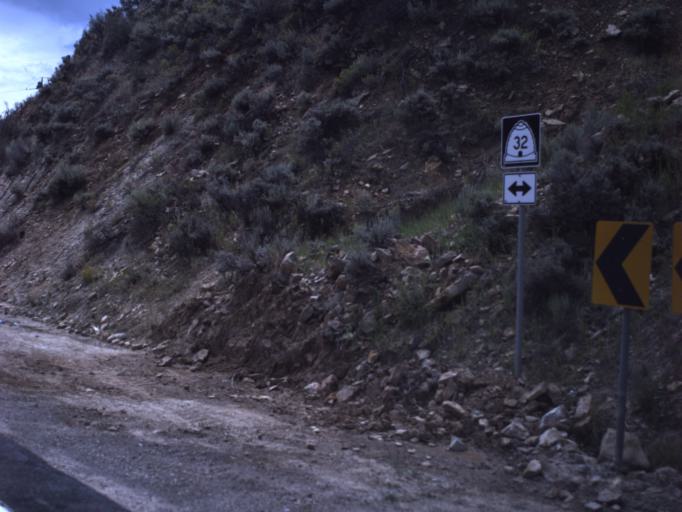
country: US
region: Utah
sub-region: Summit County
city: Oakley
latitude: 40.7529
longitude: -111.3760
